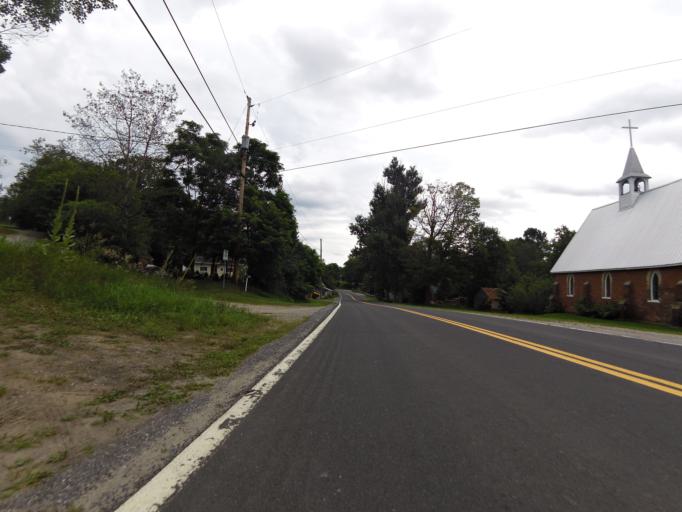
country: CA
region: Ontario
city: Perth
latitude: 44.8368
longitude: -76.5436
